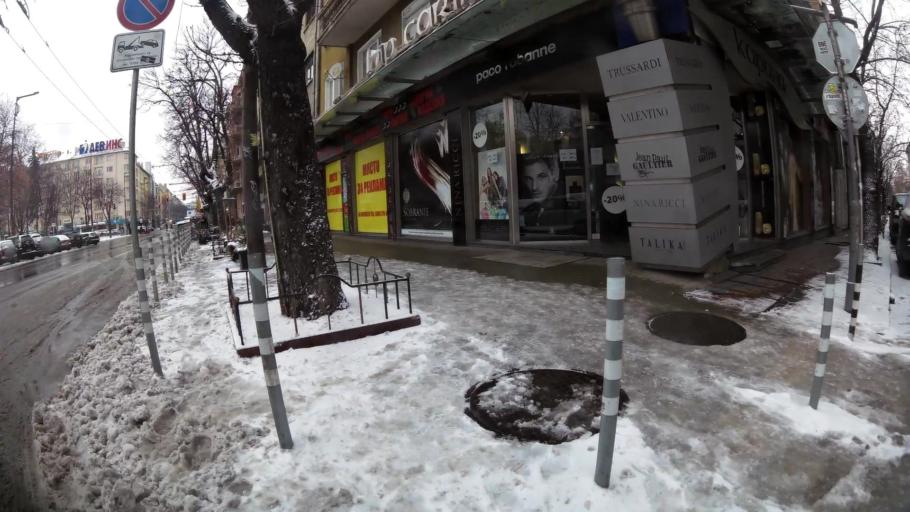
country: BG
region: Sofia-Capital
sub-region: Stolichna Obshtina
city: Sofia
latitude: 42.6890
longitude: 23.3203
